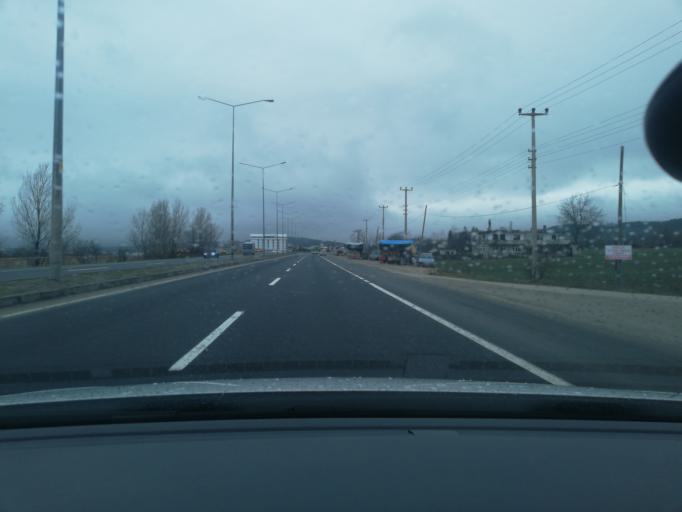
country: TR
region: Bolu
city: Bolu
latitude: 40.7306
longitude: 31.5598
